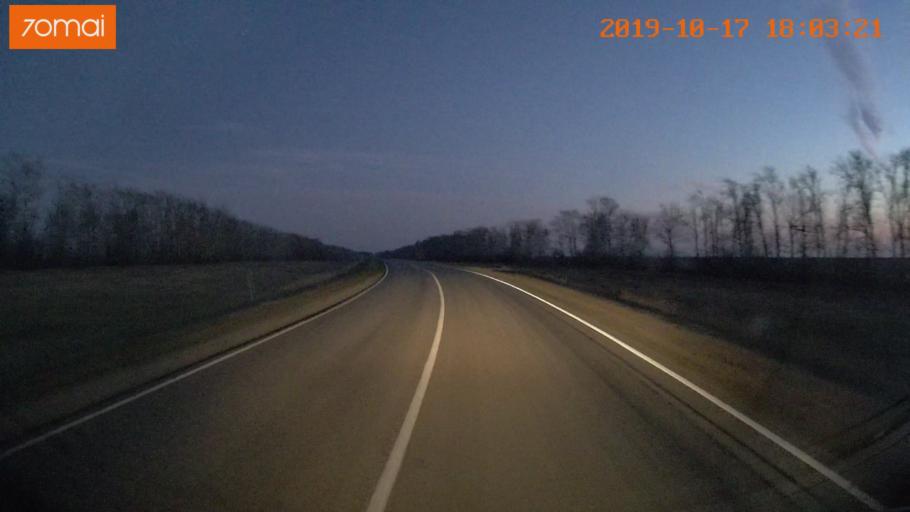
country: RU
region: Tula
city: Kurkino
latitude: 53.4952
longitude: 38.6220
